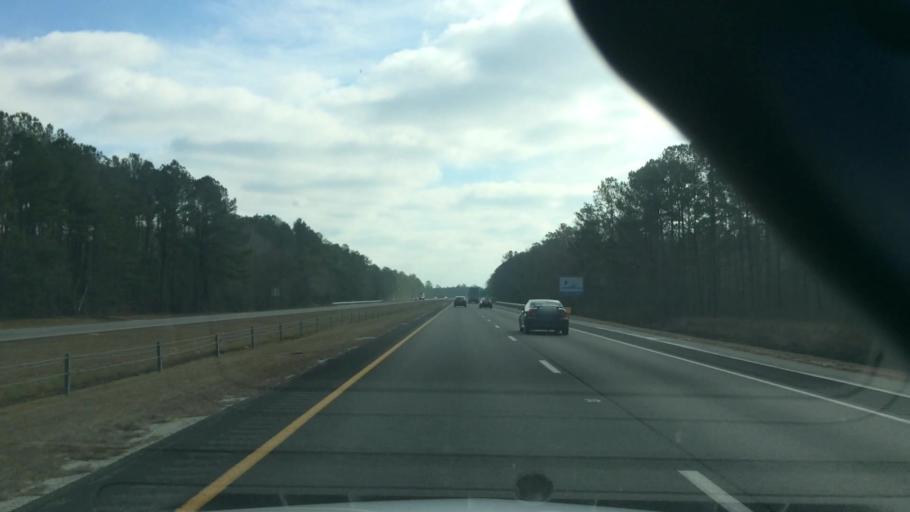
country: US
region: North Carolina
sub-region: Pender County
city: Burgaw
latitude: 34.5952
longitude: -77.9101
